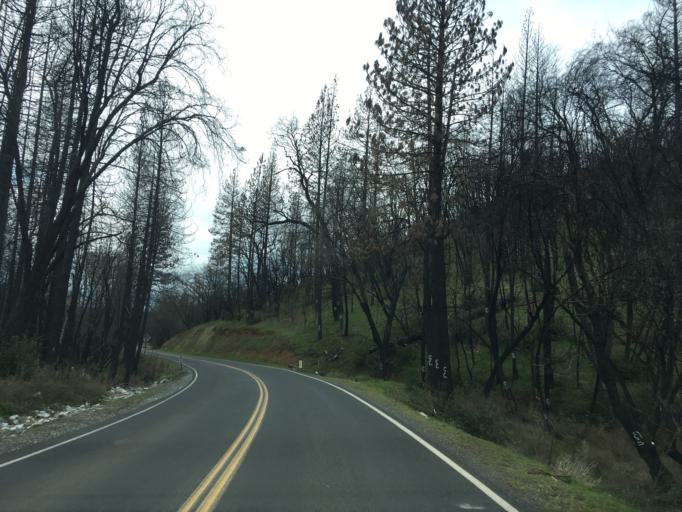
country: US
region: California
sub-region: Calaveras County
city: Mountain Ranch
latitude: 38.2363
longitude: -120.5225
